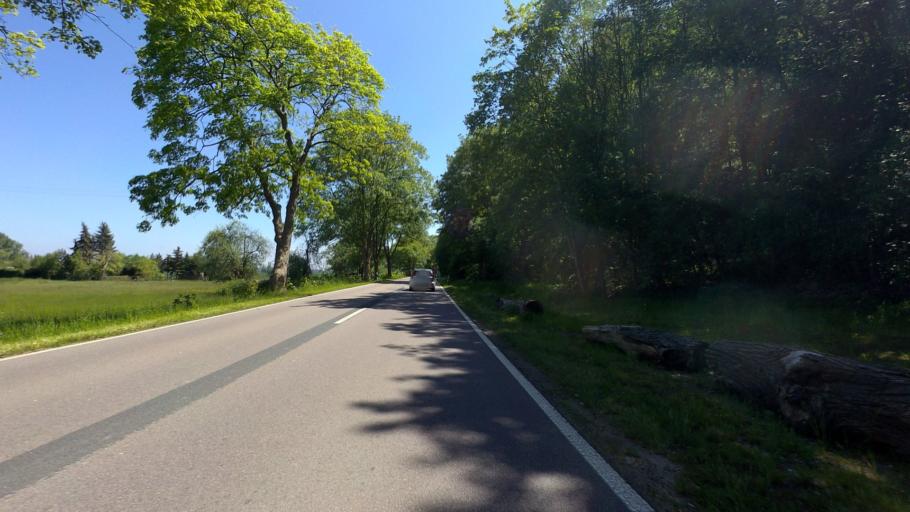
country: DE
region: Saxony
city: Coswig
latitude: 51.1082
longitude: 13.5720
